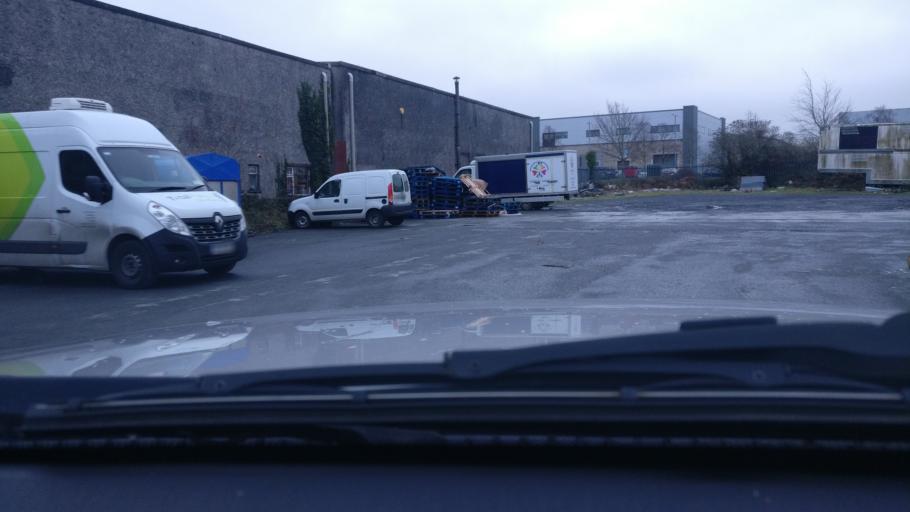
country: IE
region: Connaught
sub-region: County Galway
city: Gaillimh
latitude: 53.2929
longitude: -9.0158
